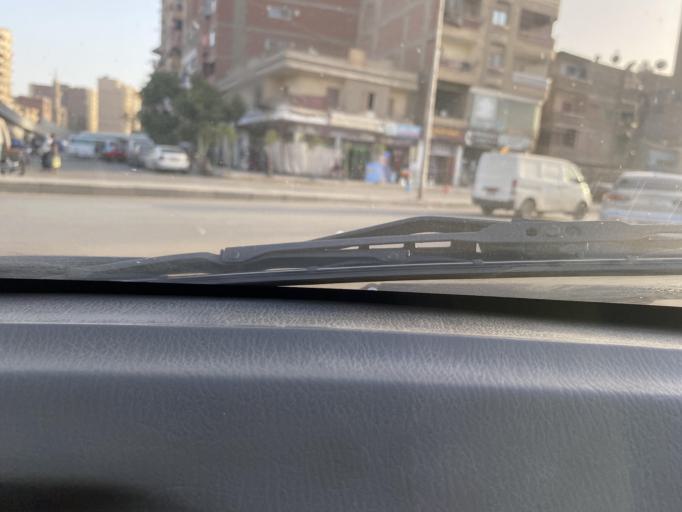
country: EG
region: Muhafazat al Qahirah
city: Cairo
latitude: 30.1140
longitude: 31.2956
